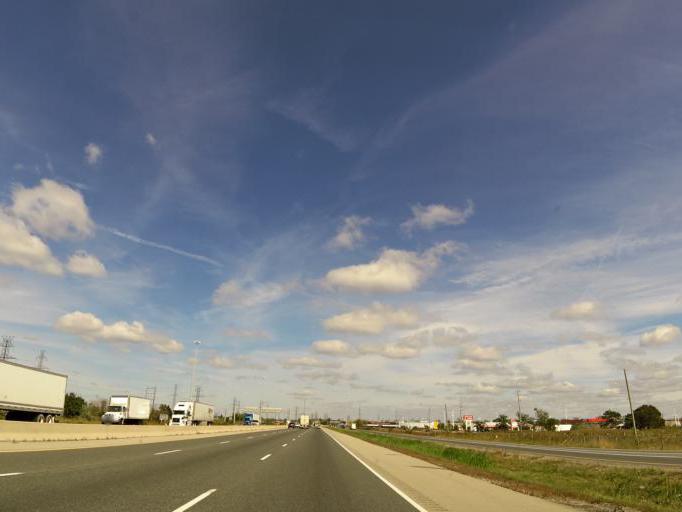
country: CA
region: Ontario
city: London
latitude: 42.9240
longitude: -81.2105
